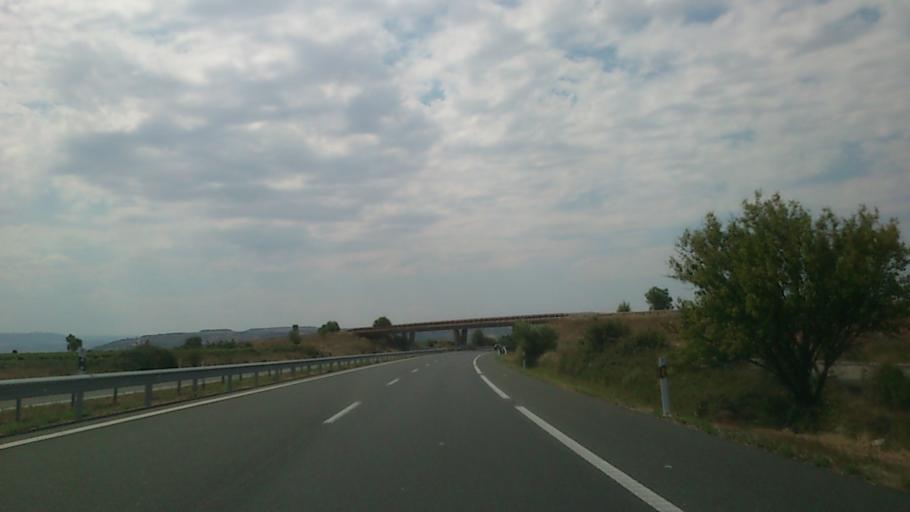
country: ES
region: La Rioja
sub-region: Provincia de La Rioja
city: Cenicero
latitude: 42.4780
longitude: -2.6697
